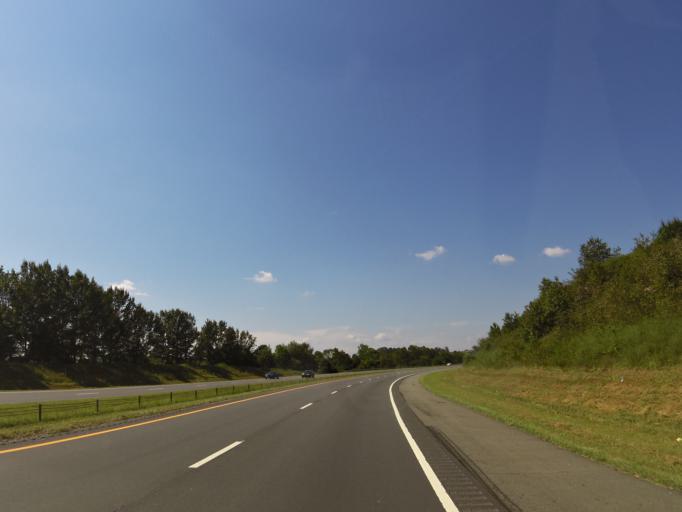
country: US
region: North Carolina
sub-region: Catawba County
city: Maiden
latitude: 35.5467
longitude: -81.2370
